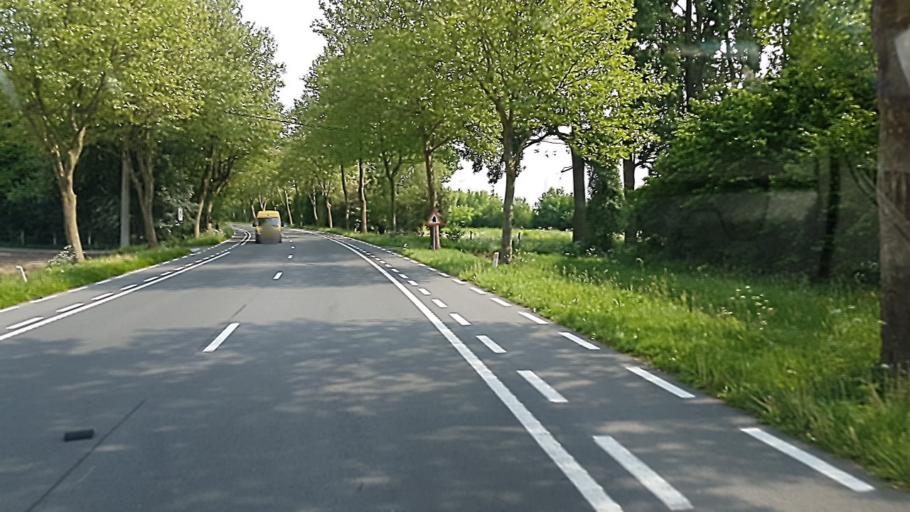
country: BE
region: Flanders
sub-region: Provincie West-Vlaanderen
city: Wevelgem
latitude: 50.8348
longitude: 3.1842
